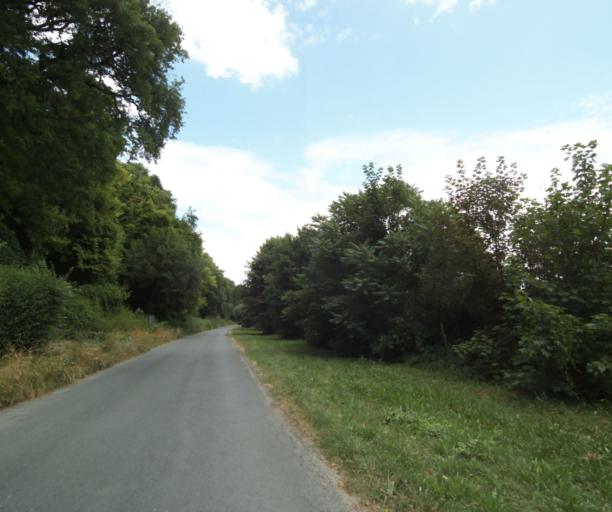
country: FR
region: Ile-de-France
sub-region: Departement de Seine-et-Marne
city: Samois-sur-Seine
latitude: 48.4396
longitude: 2.7462
